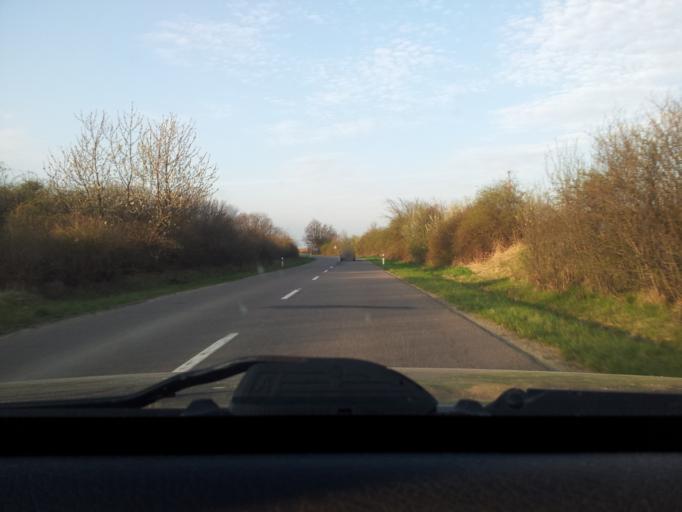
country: SK
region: Nitriansky
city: Tlmace
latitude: 48.2632
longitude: 18.4440
